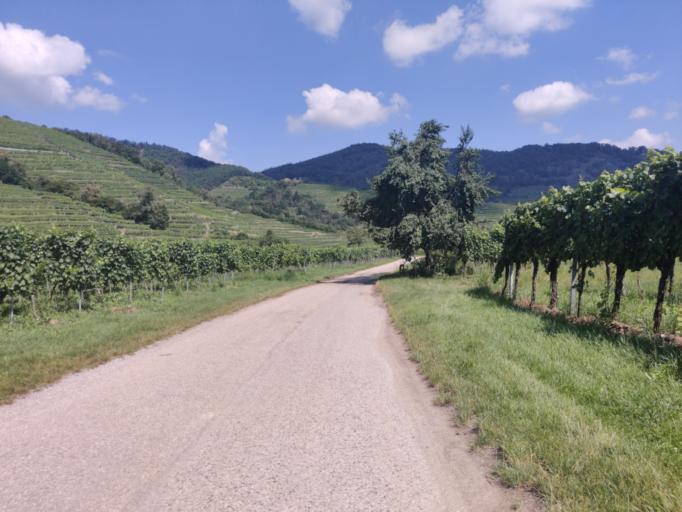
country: AT
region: Lower Austria
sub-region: Politischer Bezirk Krems
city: Durnstein
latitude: 48.4094
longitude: 15.4880
